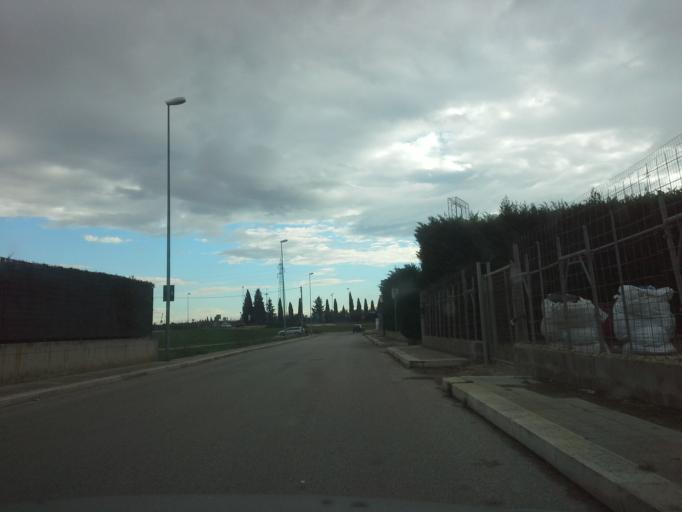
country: IT
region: Apulia
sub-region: Provincia di Bari
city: Adelfia
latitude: 41.0052
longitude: 16.8813
